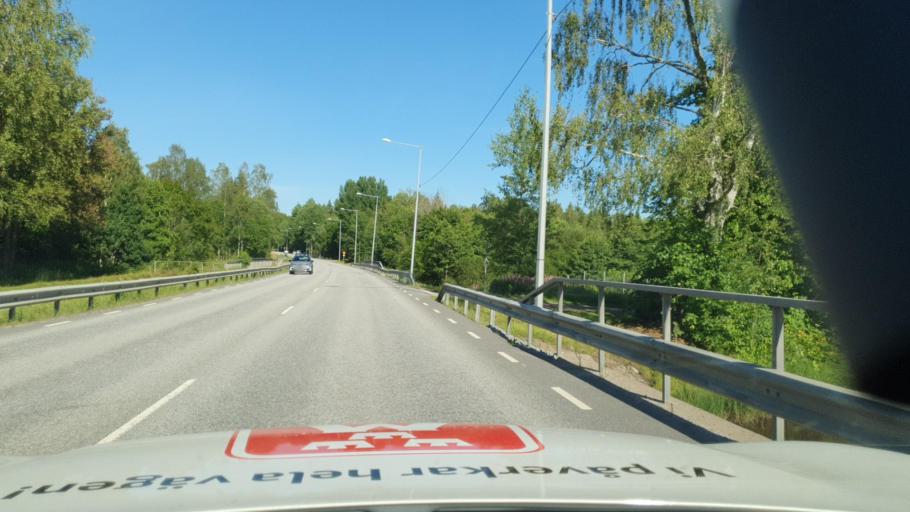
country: SE
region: OErebro
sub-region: Karlskoga Kommun
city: Karlskoga
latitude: 59.3377
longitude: 14.5364
